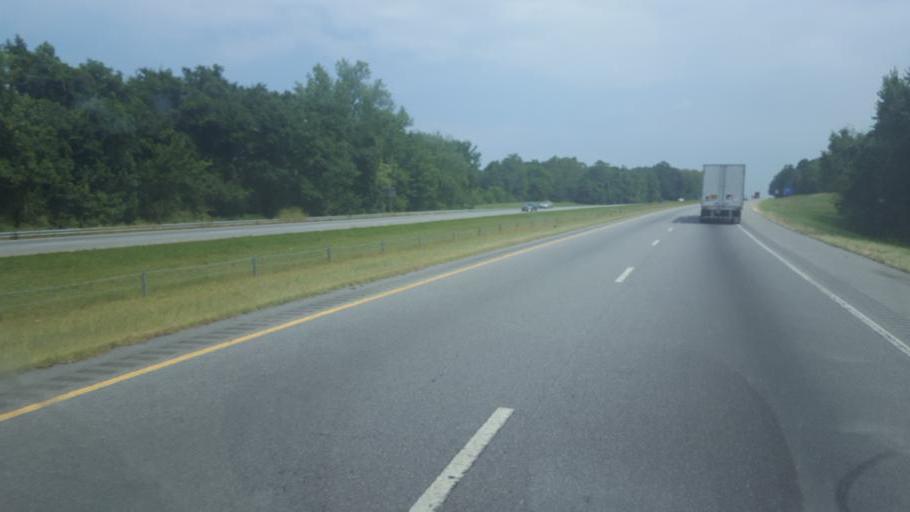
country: US
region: North Carolina
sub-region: Iredell County
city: Statesville
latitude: 35.9940
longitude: -80.8391
